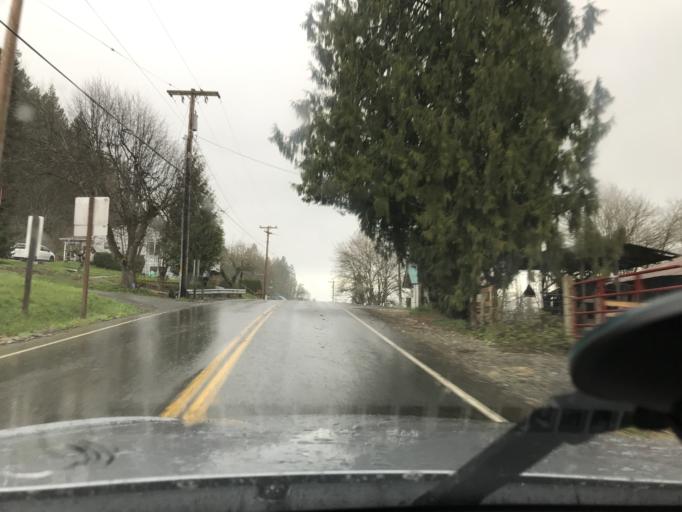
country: US
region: Washington
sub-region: King County
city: Ames Lake
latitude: 47.6728
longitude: -121.9783
